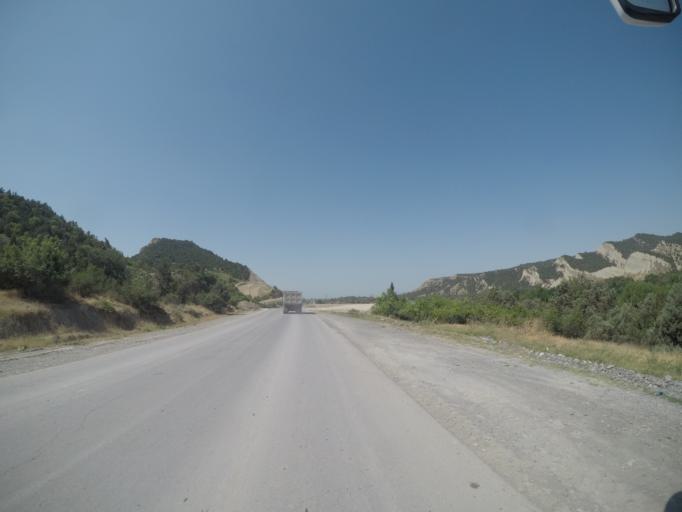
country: AZ
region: Agdas
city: Agdas
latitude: 40.7206
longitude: 47.5618
